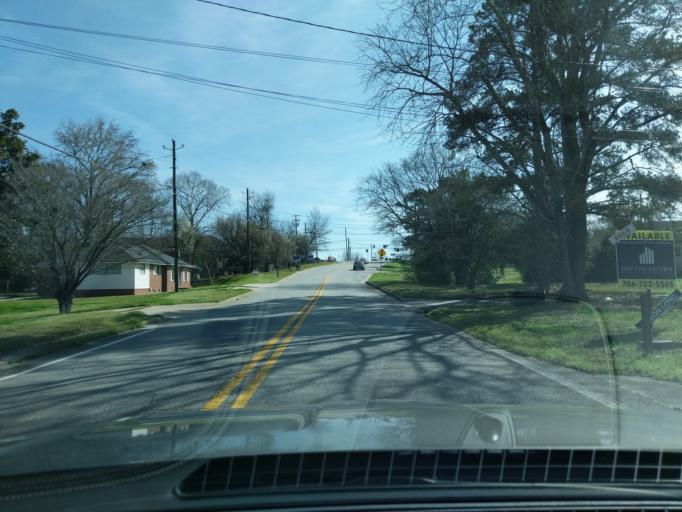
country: US
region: Georgia
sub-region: Columbia County
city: Evans
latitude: 33.5337
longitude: -82.1327
